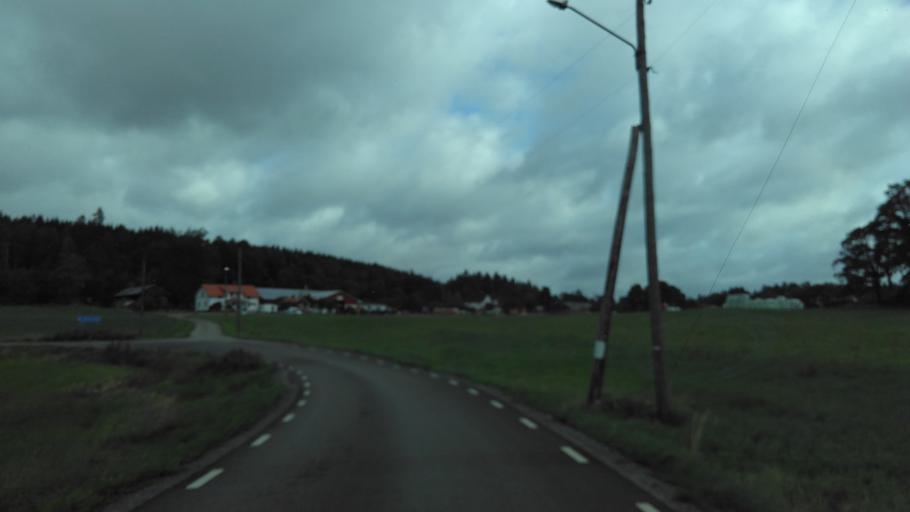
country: SE
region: Vaestra Goetaland
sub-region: Marks Kommun
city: Fritsla
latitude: 57.5701
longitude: 12.7839
